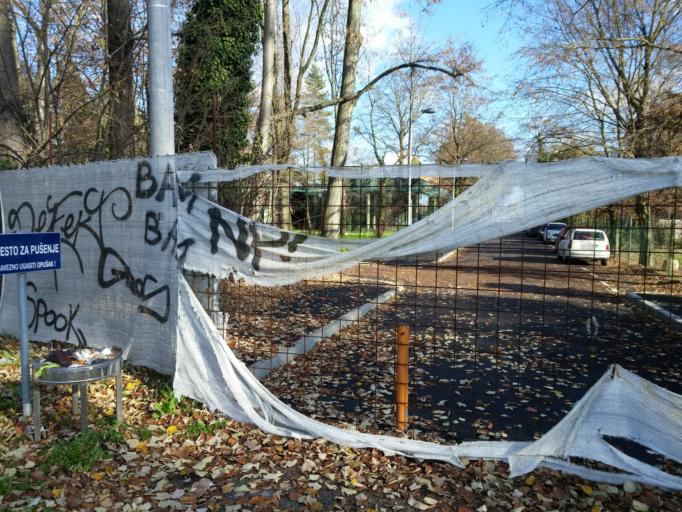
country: HR
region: Grad Zagreb
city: Dubrava
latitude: 45.8277
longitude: 16.0285
